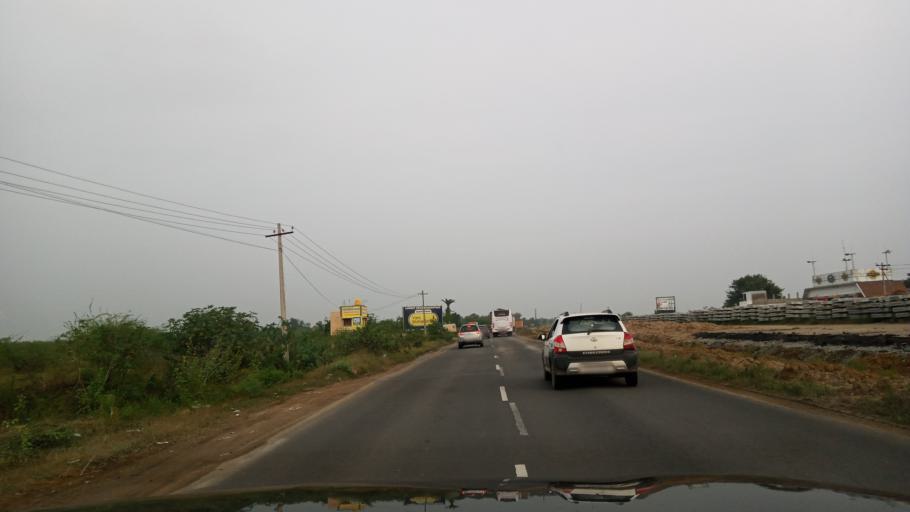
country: IN
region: Tamil Nadu
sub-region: Vellore
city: Walajapet
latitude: 12.9024
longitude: 79.4792
